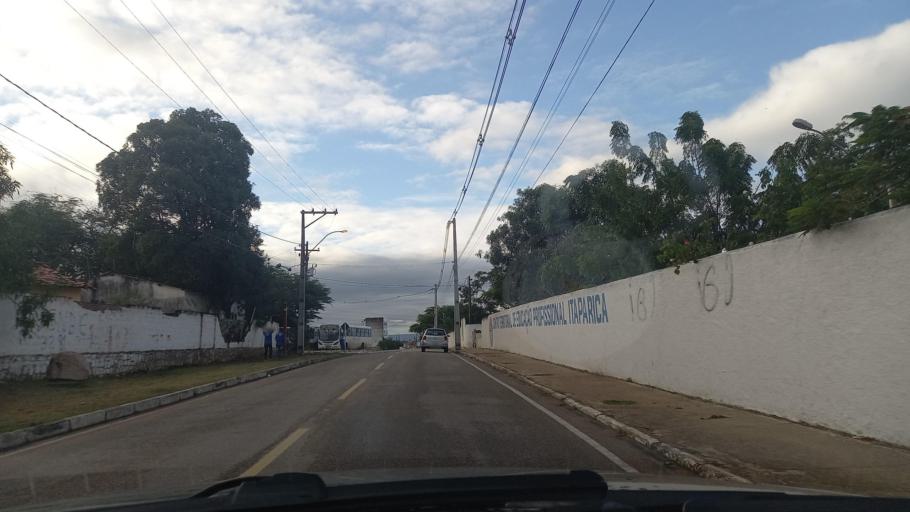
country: BR
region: Bahia
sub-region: Paulo Afonso
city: Paulo Afonso
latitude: -9.3908
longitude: -38.2320
